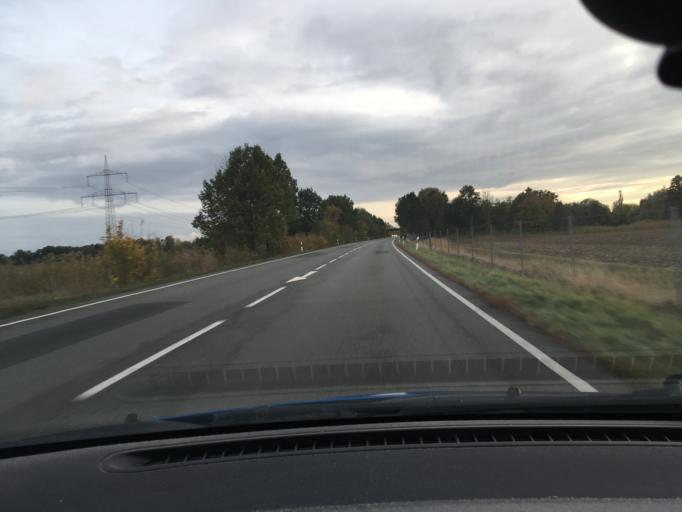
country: DE
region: Lower Saxony
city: Handorf
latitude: 53.3764
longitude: 10.3480
